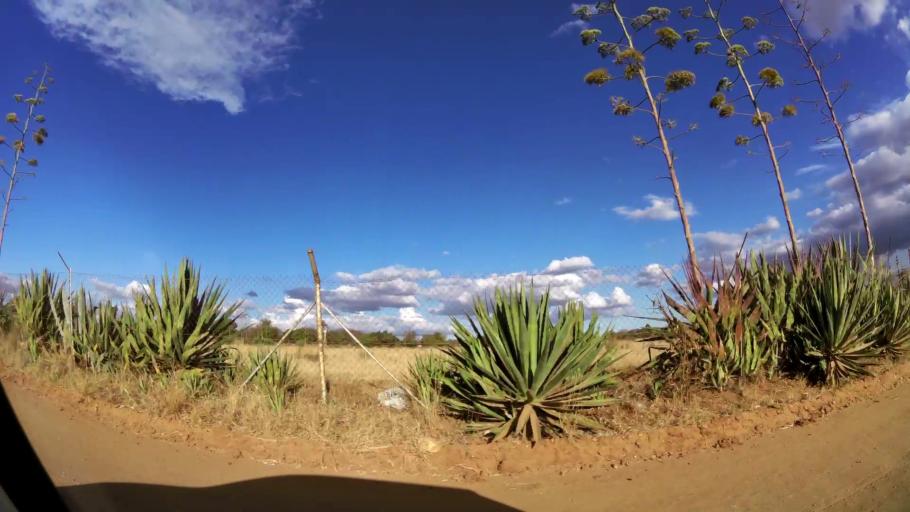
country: ZA
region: Limpopo
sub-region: Capricorn District Municipality
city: Polokwane
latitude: -23.9325
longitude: 29.4307
